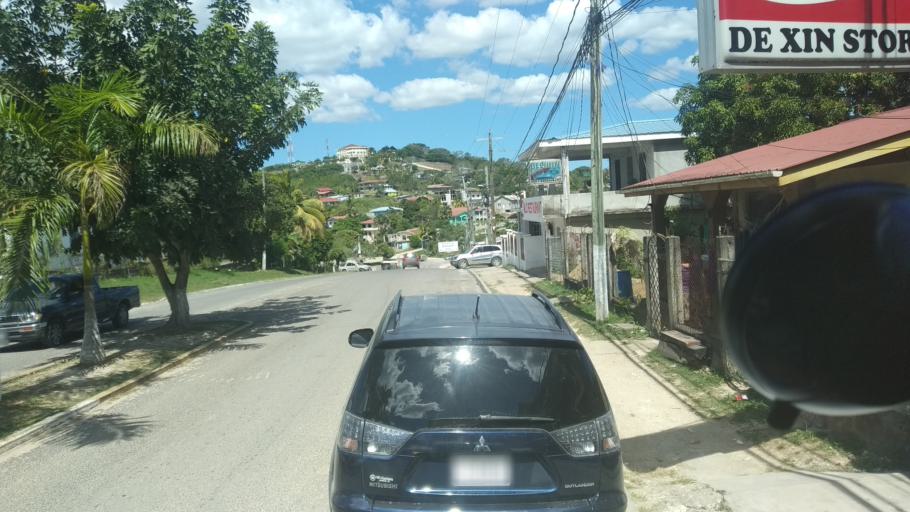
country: BZ
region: Cayo
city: Benque Viejo del Carmen
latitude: 17.0740
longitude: -89.1355
